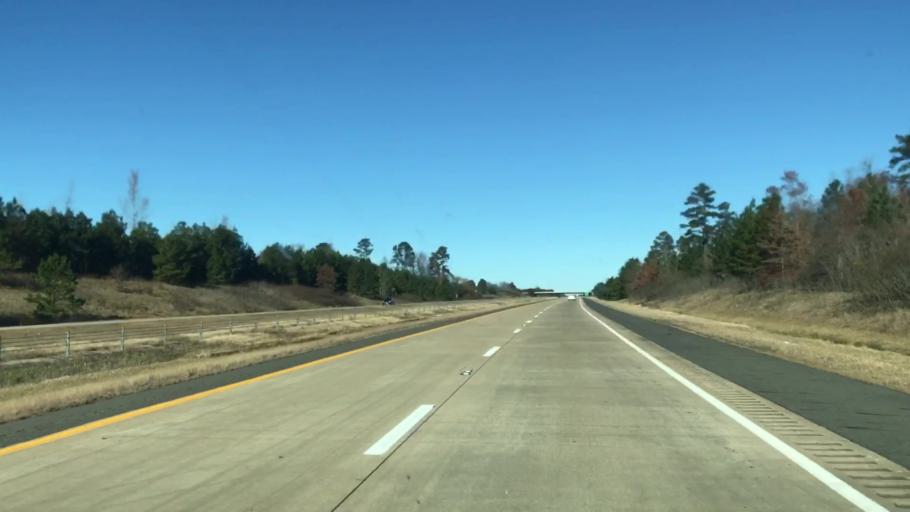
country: US
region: Texas
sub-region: Bowie County
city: Texarkana
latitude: 33.3089
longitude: -93.9380
